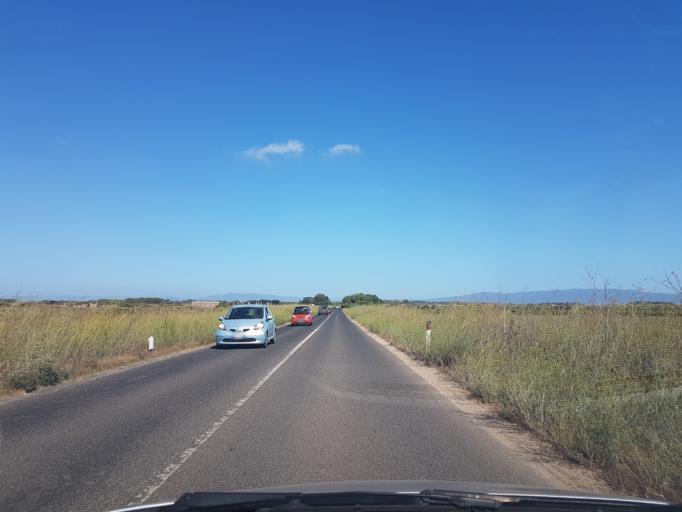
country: IT
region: Sardinia
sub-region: Provincia di Oristano
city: Cabras
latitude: 39.9168
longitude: 8.4749
